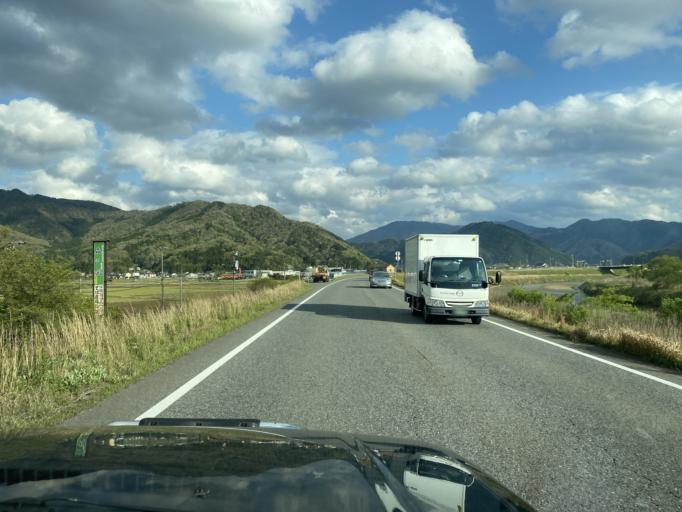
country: JP
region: Hyogo
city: Toyooka
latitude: 35.4847
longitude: 134.8600
